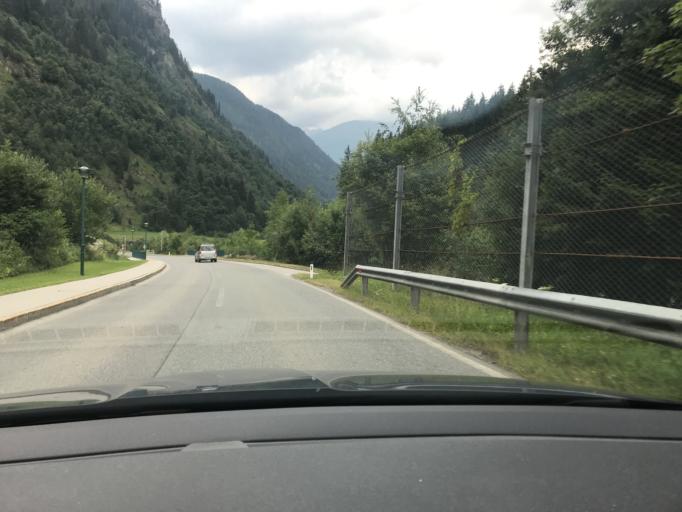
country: AT
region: Tyrol
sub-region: Politischer Bezirk Lienz
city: Hopfgarten in Defereggen
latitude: 46.9213
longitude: 12.5235
